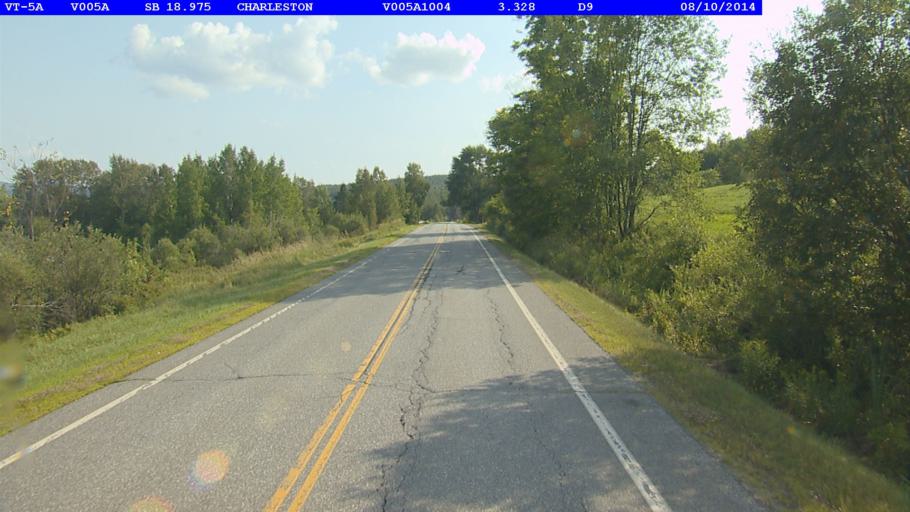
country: US
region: Vermont
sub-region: Orleans County
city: Newport
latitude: 44.8783
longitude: -72.0601
